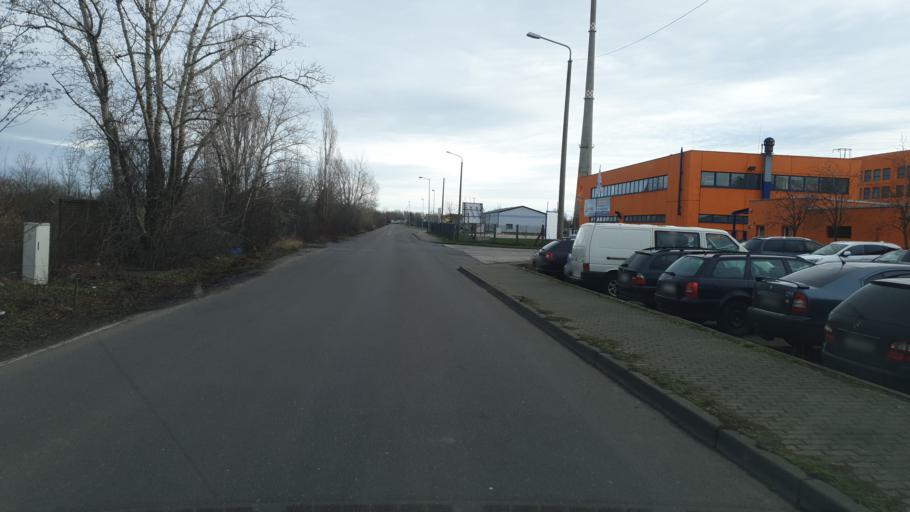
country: DE
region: Saxony
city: Kitzen
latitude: 51.2498
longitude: 12.2643
